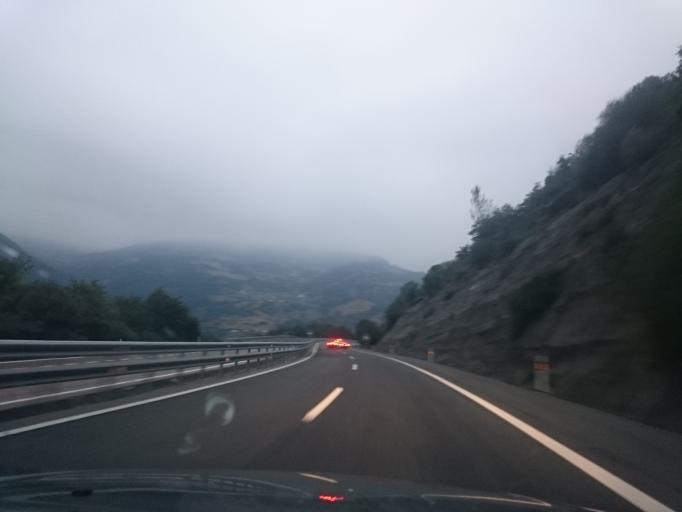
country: ES
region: Asturias
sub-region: Province of Asturias
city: Pola de Lena
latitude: 43.0559
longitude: -5.8213
